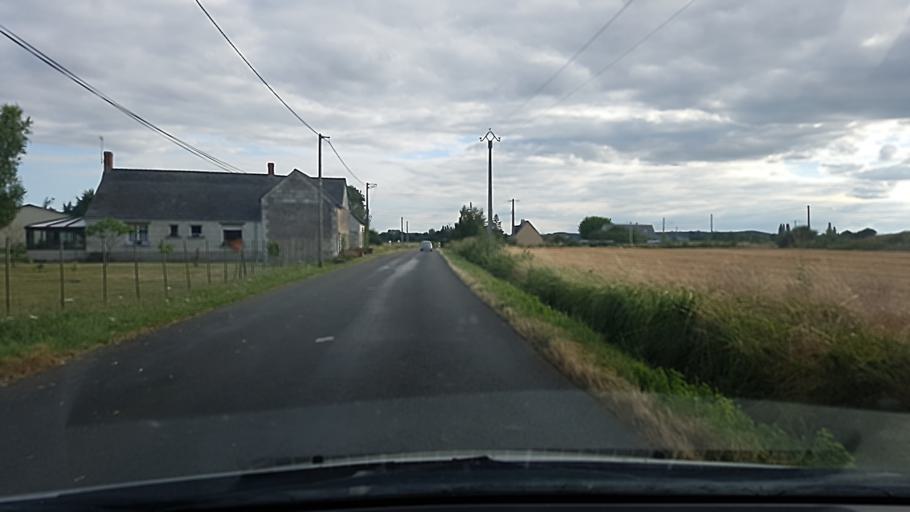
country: FR
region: Pays de la Loire
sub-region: Departement de Maine-et-Loire
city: Saint-Mathurin-sur-Loire
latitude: 47.4284
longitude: -0.3004
